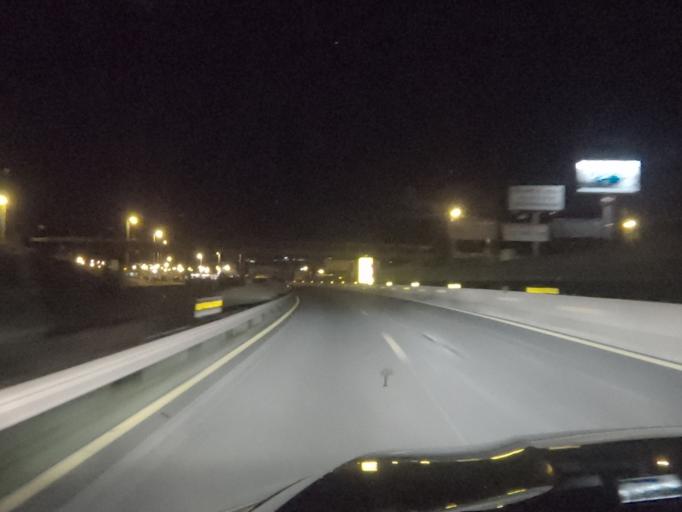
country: PT
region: Porto
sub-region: Maia
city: Pedroucos
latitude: 41.1999
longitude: -8.5722
